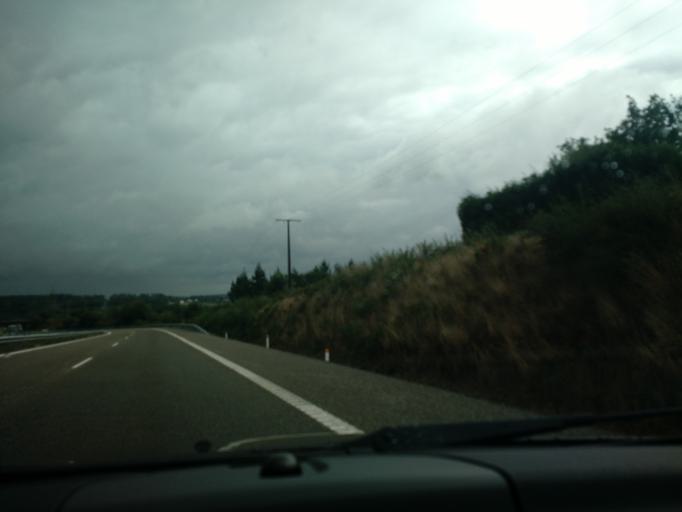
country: ES
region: Galicia
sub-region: Provincia da Coruna
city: Oroso
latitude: 42.9625
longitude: -8.4557
